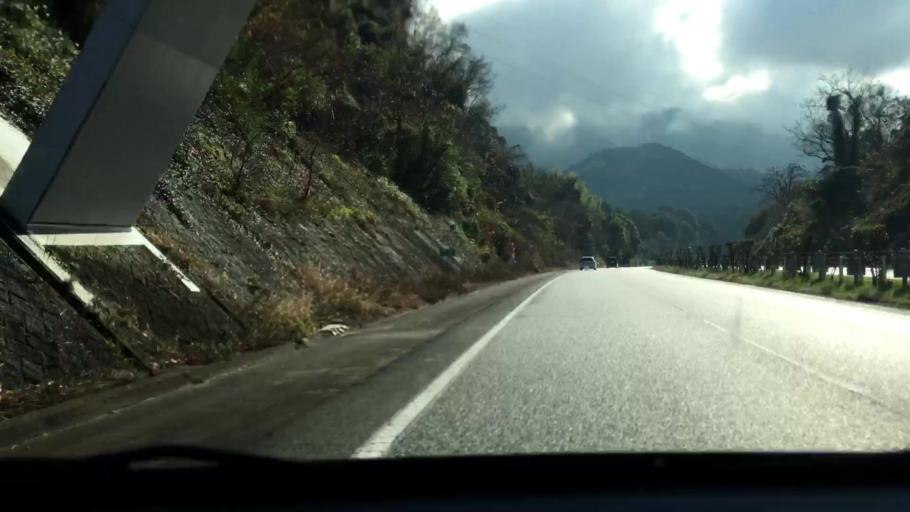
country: JP
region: Kumamoto
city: Matsubase
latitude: 32.5551
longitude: 130.6950
